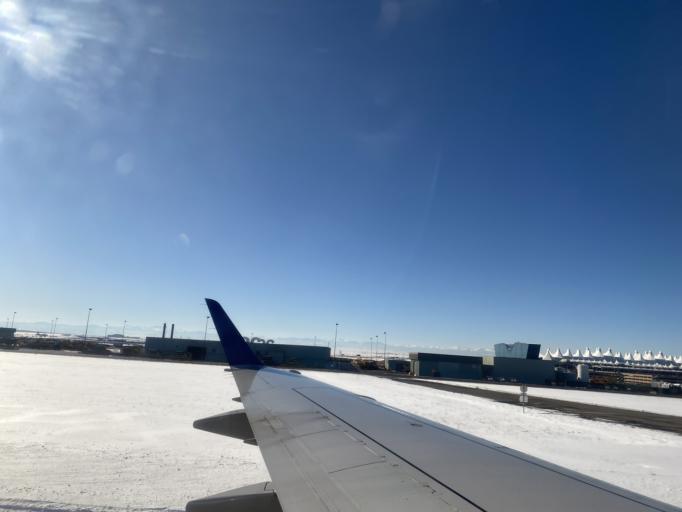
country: US
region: Colorado
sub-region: Weld County
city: Lochbuie
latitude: 39.8444
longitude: -104.6625
